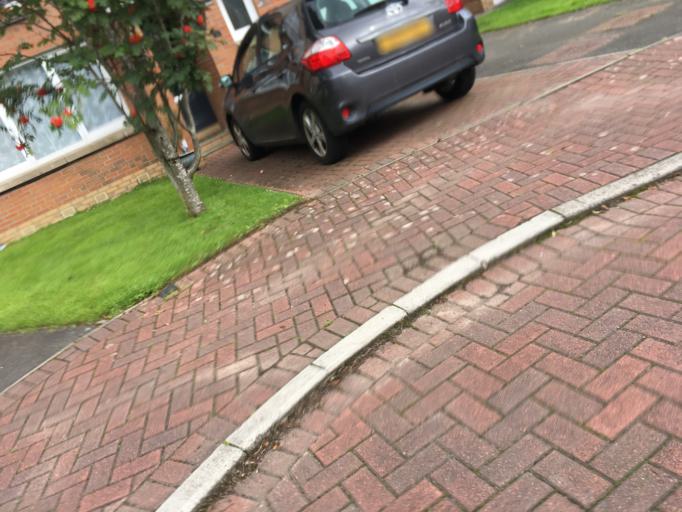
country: GB
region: Scotland
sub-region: West Lothian
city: Livingston
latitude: 55.8704
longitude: -3.5106
